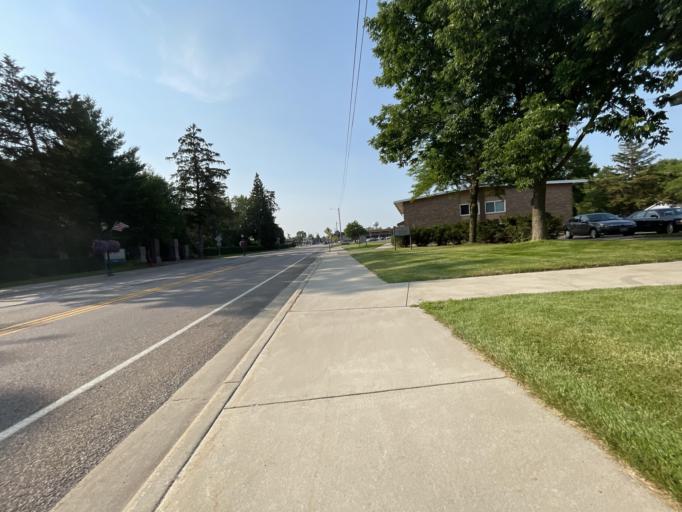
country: US
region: Minnesota
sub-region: Stearns County
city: Saint Joseph
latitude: 45.5627
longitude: -94.3170
